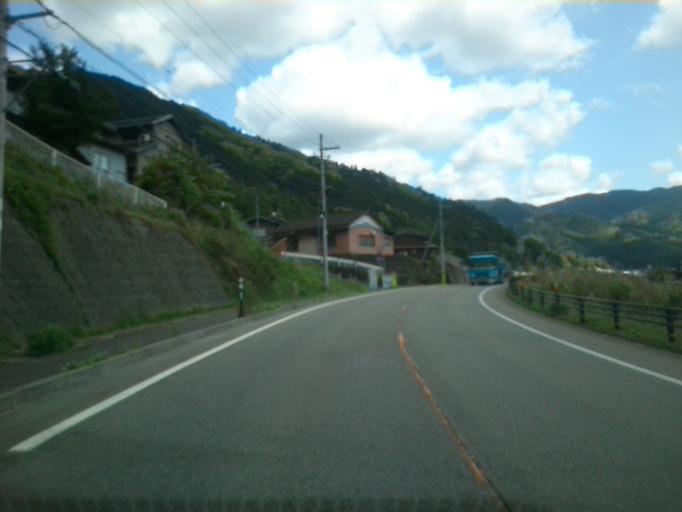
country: JP
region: Kyoto
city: Fukuchiyama
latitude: 35.4283
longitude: 135.0047
